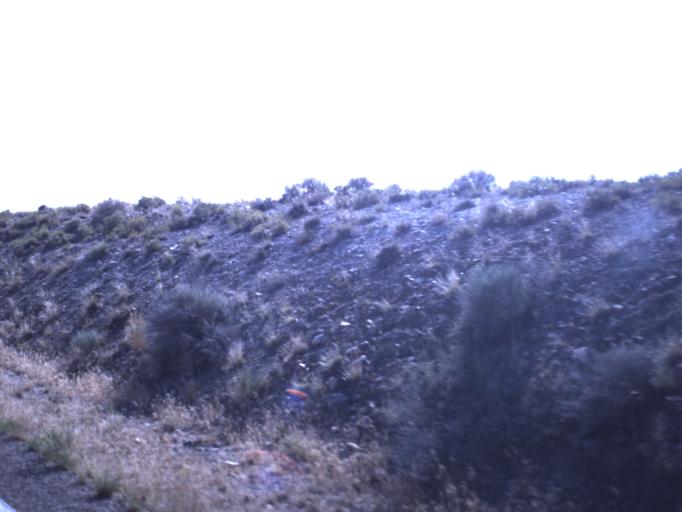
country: US
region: Utah
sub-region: Beaver County
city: Milford
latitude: 38.7414
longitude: -112.9578
